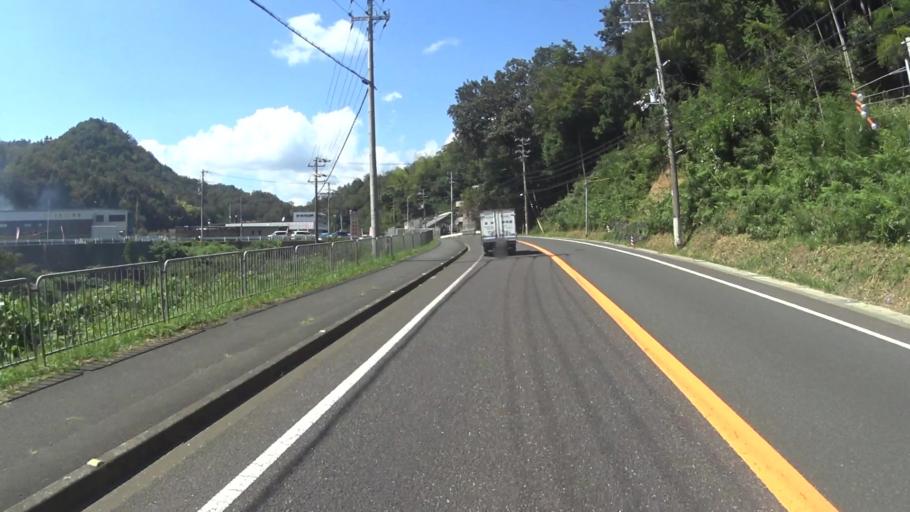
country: JP
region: Kyoto
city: Maizuru
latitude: 35.4482
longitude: 135.2882
